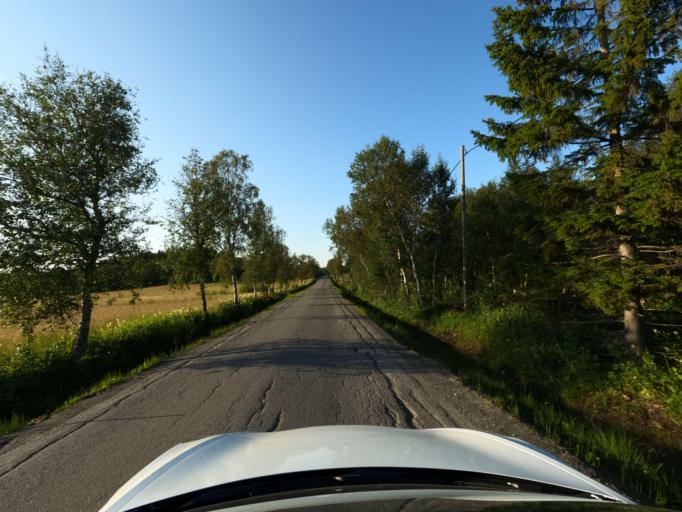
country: NO
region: Troms
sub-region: Skanland
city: Evenskjer
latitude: 68.4671
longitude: 16.7016
